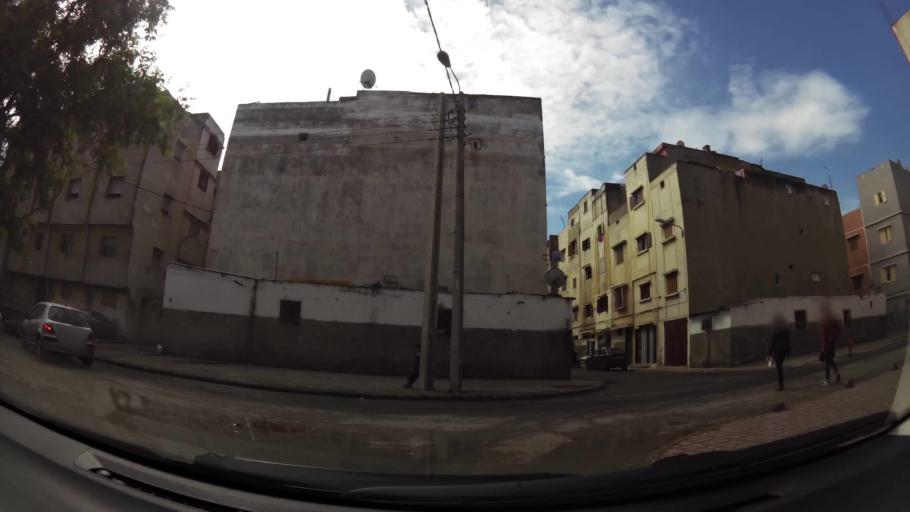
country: MA
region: Grand Casablanca
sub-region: Casablanca
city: Casablanca
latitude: 33.5711
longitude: -7.6732
